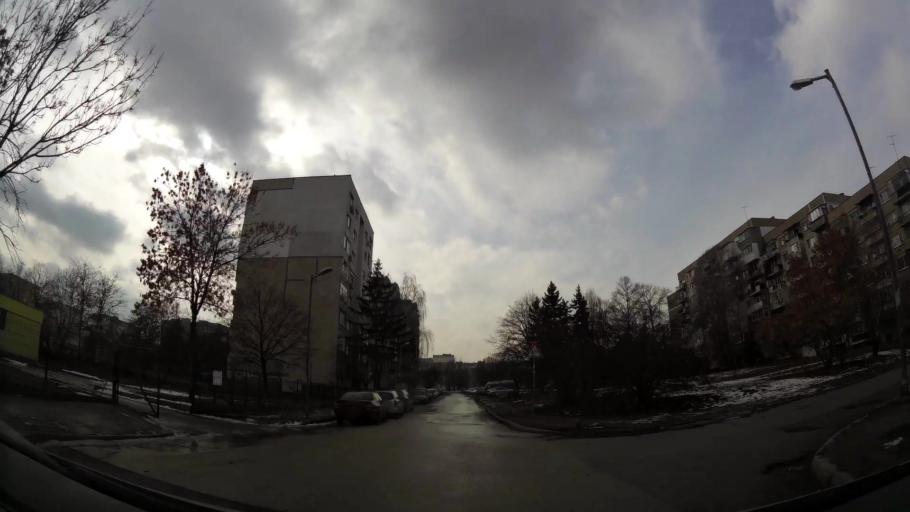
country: BG
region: Sofiya
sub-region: Obshtina Bozhurishte
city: Bozhurishte
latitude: 42.7212
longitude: 23.2461
